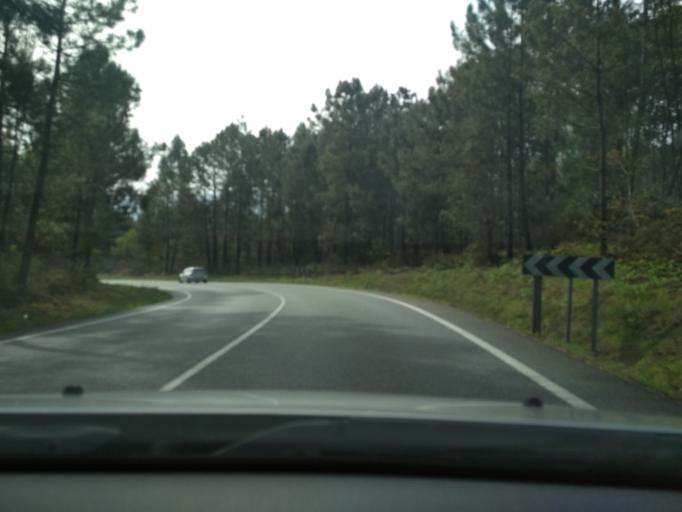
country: ES
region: Galicia
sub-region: Provincia de Pontevedra
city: Catoira
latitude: 42.6735
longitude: -8.7143
